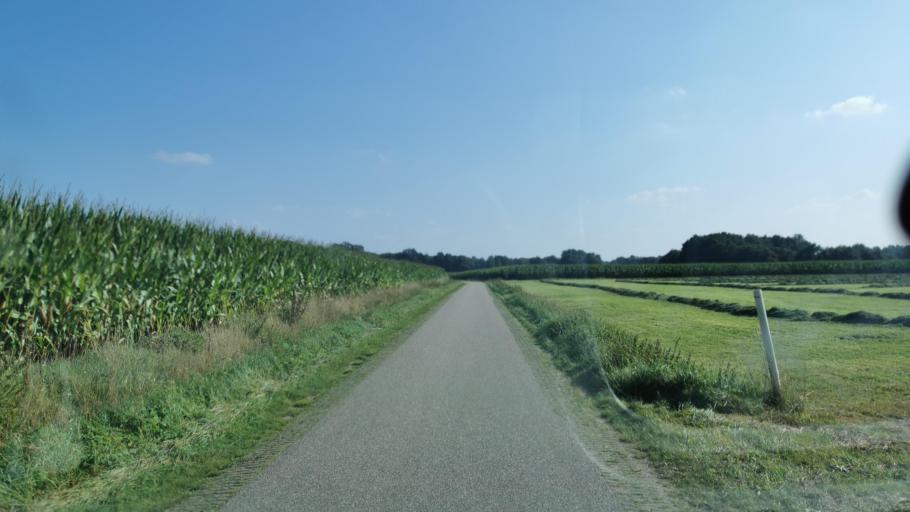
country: DE
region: Lower Saxony
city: Lage
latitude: 52.4007
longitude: 6.9482
